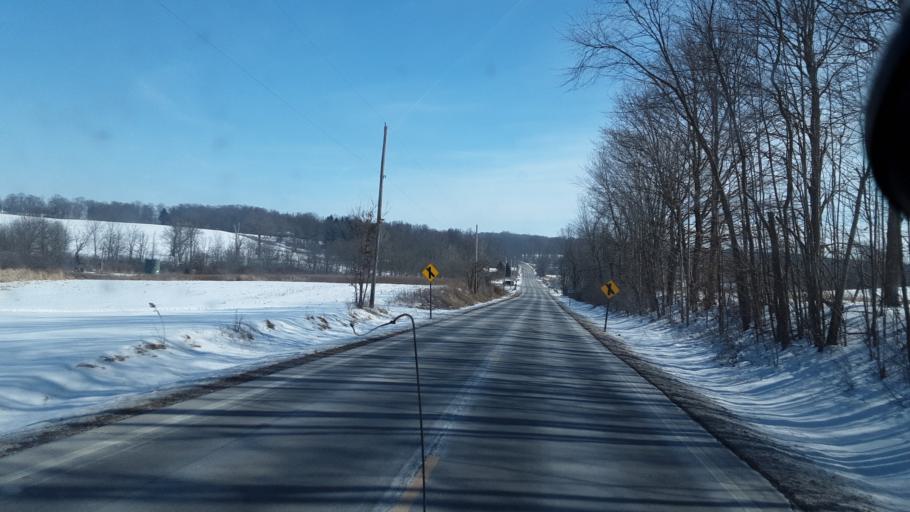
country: US
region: Ohio
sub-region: Mahoning County
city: Sebring
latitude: 40.9469
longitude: -80.9495
